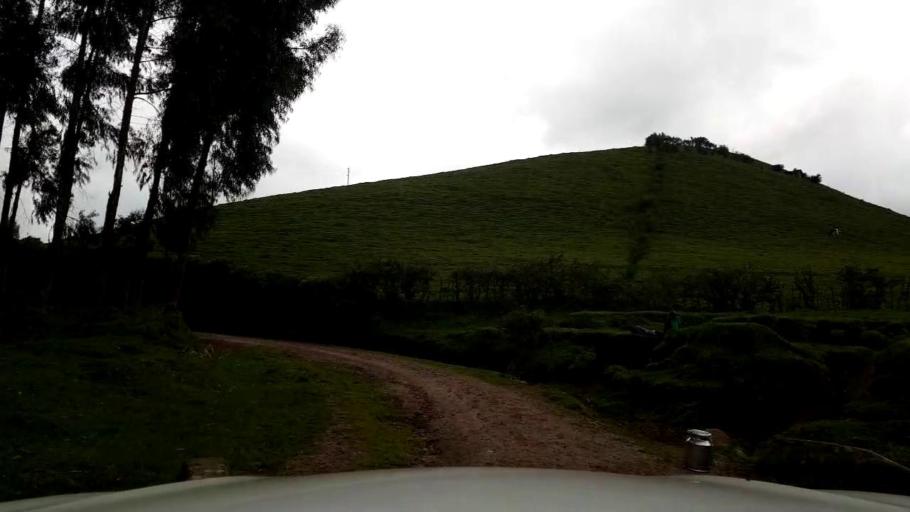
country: RW
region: Western Province
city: Gisenyi
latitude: -1.6867
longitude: 29.4194
